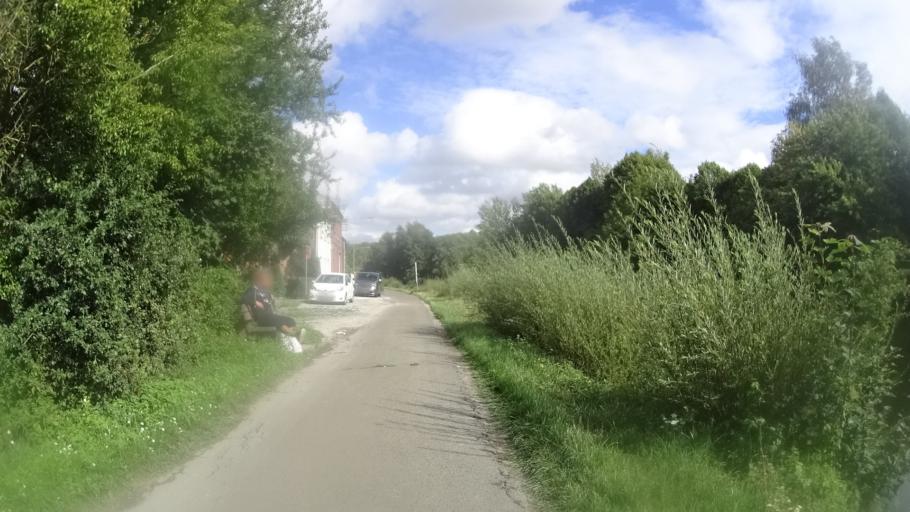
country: BE
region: Wallonia
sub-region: Province du Hainaut
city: Merbes-le-Chateau
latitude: 50.3139
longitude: 4.1875
